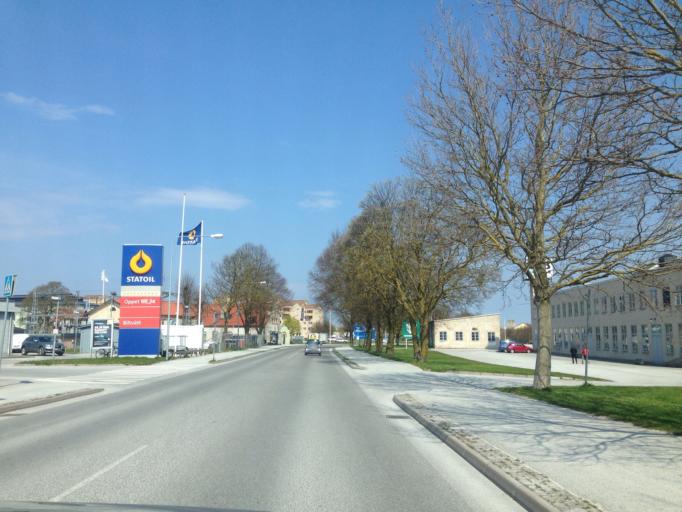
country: SE
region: Gotland
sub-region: Gotland
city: Visby
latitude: 57.6295
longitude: 18.2879
